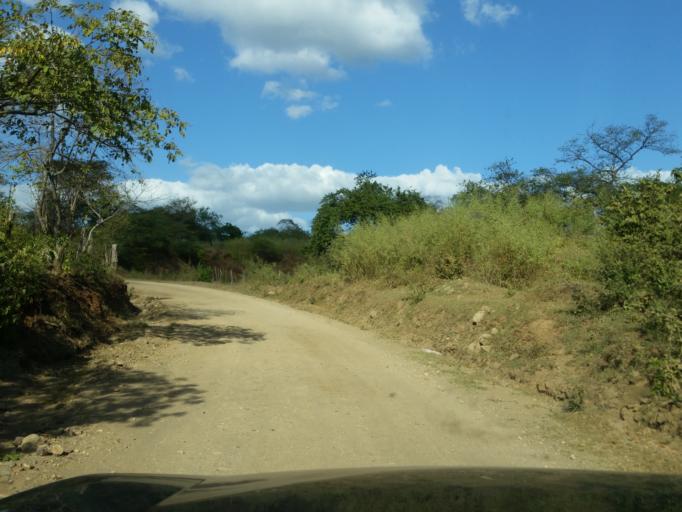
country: NI
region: Managua
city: Carlos Fonseca Amador
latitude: 11.9202
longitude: -86.5942
